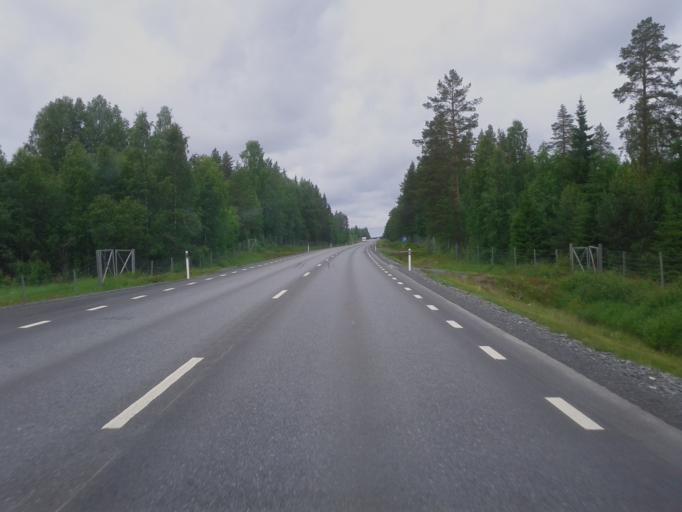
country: SE
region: Vaesterbotten
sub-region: Skelleftea Kommun
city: Forsbacka
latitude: 64.8432
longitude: 20.5035
